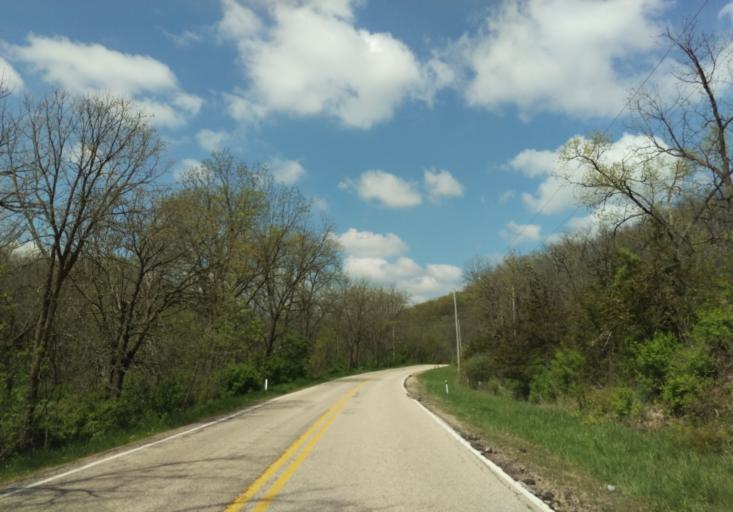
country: US
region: Wisconsin
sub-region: Dane County
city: Mount Horeb
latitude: 43.0564
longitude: -89.7616
